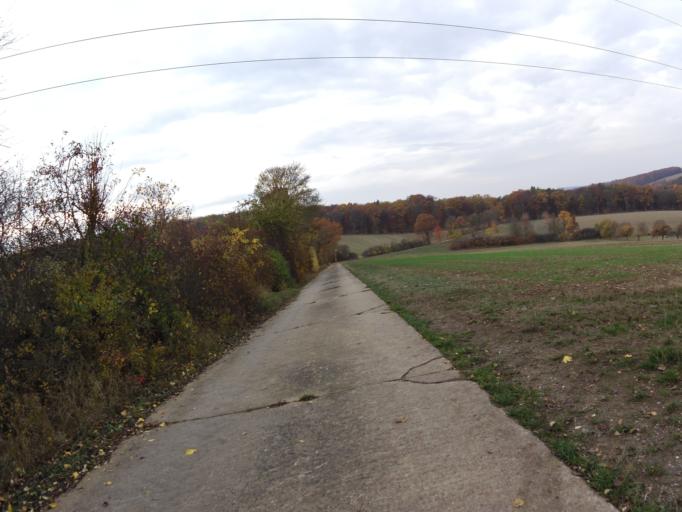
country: DE
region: Bavaria
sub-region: Regierungsbezirk Unterfranken
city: Kist
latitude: 49.7446
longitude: 9.8324
